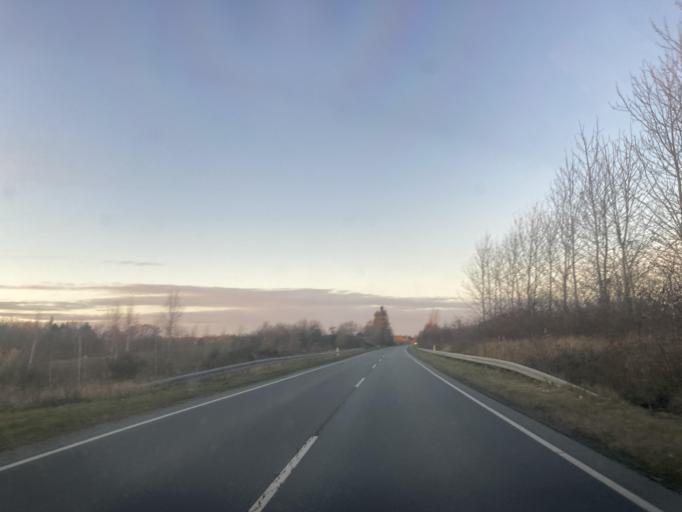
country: DK
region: Capital Region
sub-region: Gribskov Kommune
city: Graested
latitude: 56.0503
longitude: 12.2800
